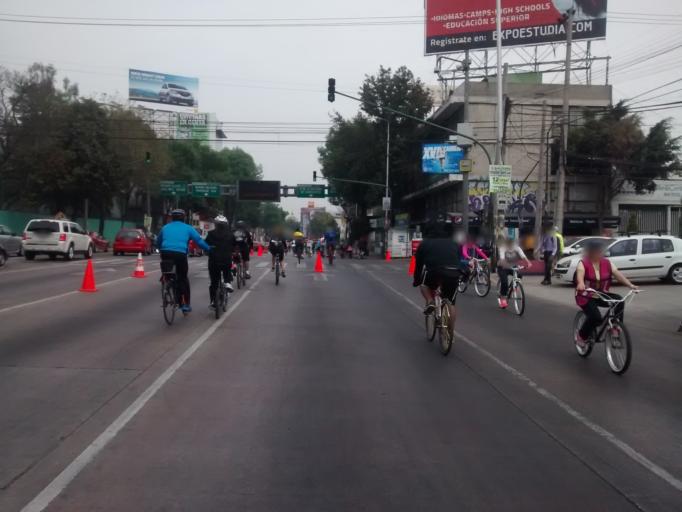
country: MX
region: Mexico City
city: Benito Juarez
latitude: 19.4024
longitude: -99.1790
